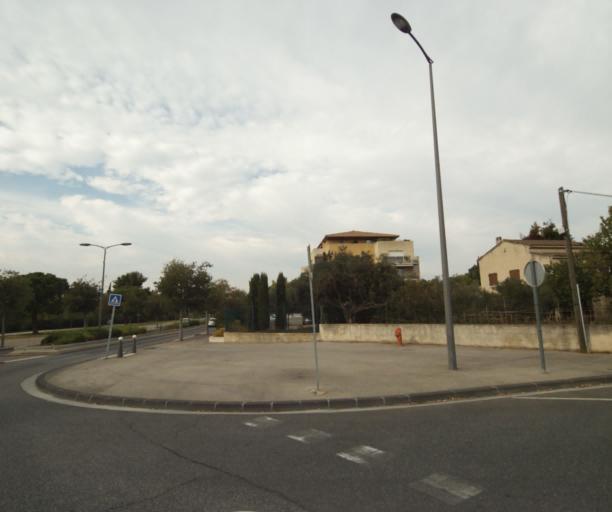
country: FR
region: Provence-Alpes-Cote d'Azur
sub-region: Departement des Bouches-du-Rhone
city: Marignane
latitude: 43.4154
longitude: 5.2042
